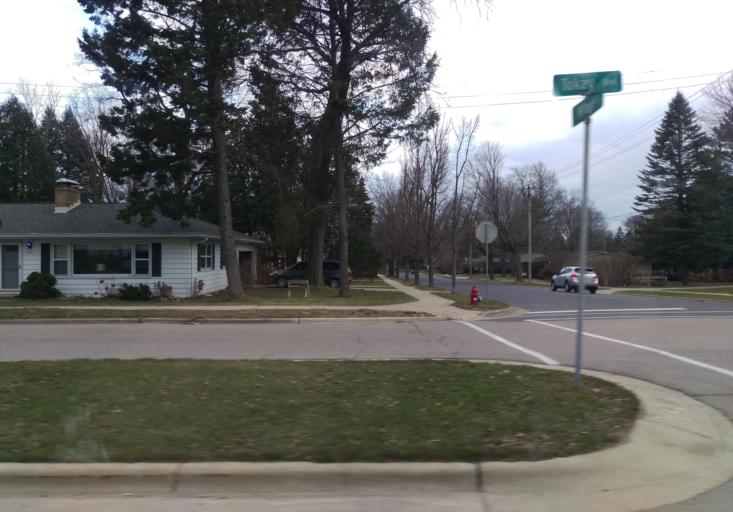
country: US
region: Wisconsin
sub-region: Dane County
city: Shorewood Hills
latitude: 43.0537
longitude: -89.4585
